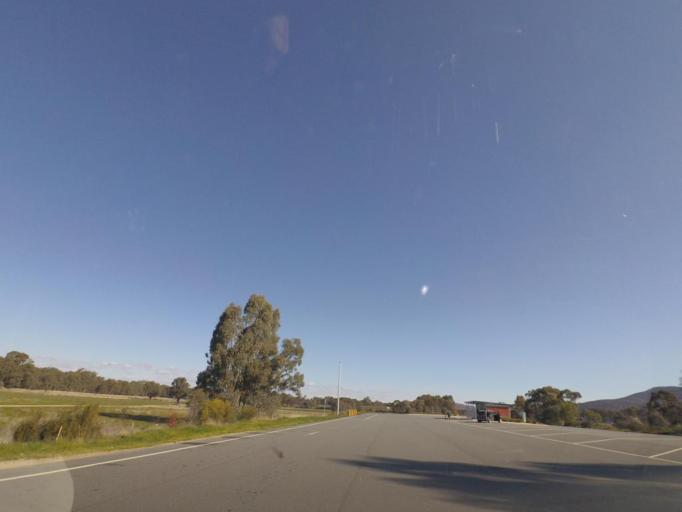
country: AU
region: Victoria
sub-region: Wangaratta
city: Wangaratta
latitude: -36.4235
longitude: 146.2637
